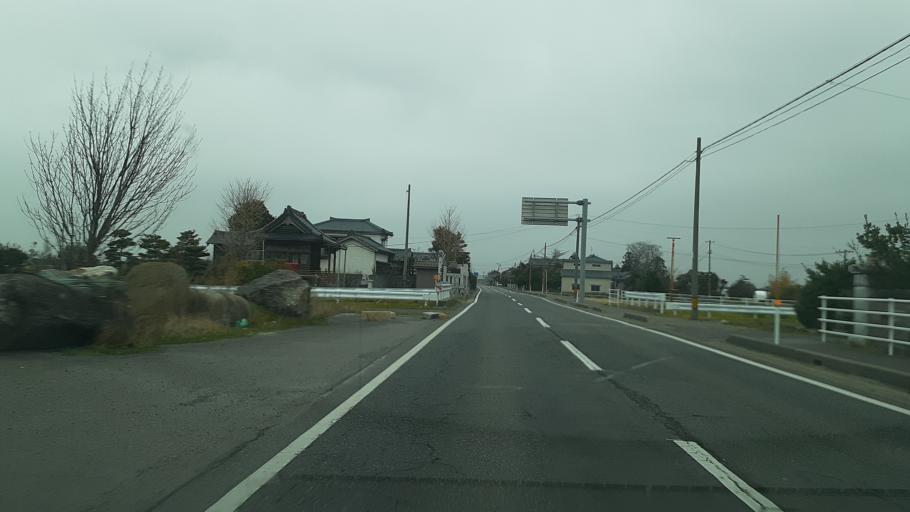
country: JP
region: Niigata
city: Kameda-honcho
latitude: 37.8599
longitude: 139.0605
